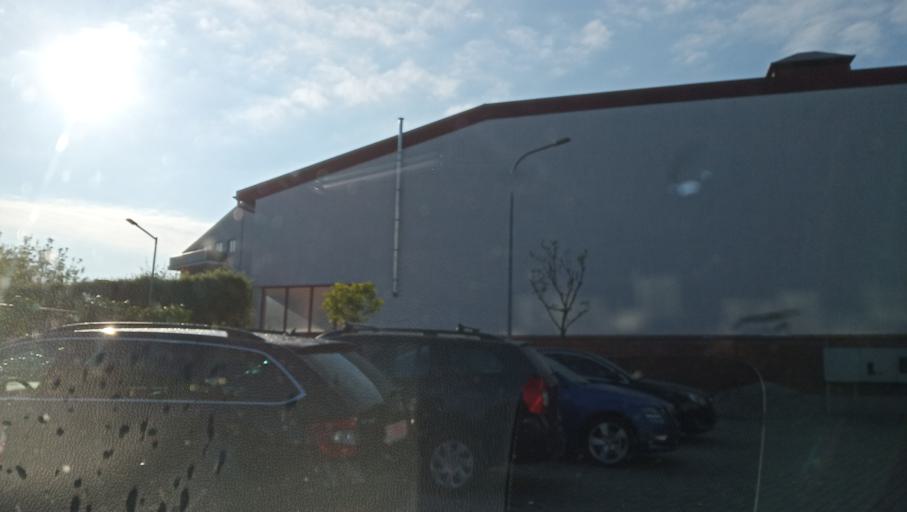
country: RO
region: Timis
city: Timisoara
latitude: 45.7403
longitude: 21.2336
